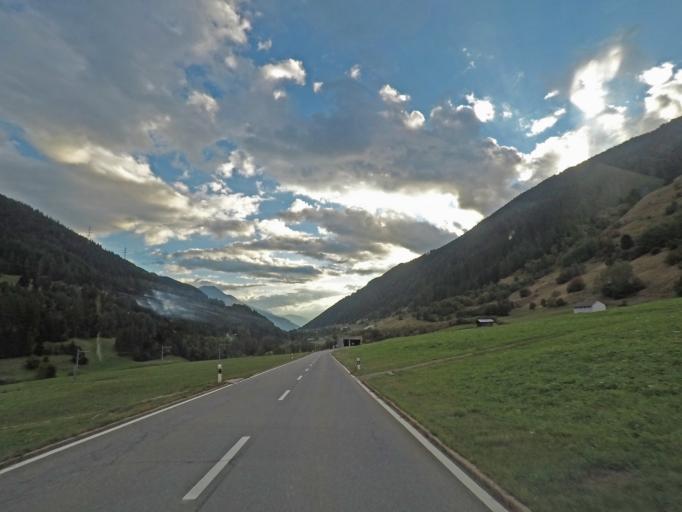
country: CH
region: Valais
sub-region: Goms District
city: Fiesch
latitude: 46.4383
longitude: 8.1977
